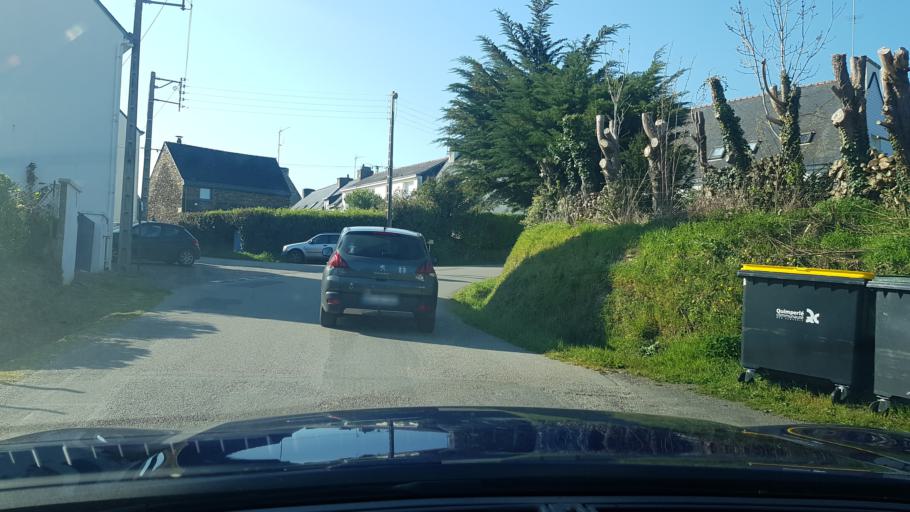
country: FR
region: Brittany
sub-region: Departement du Finistere
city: Moelan-sur-Mer
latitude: 47.7811
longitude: -3.6280
